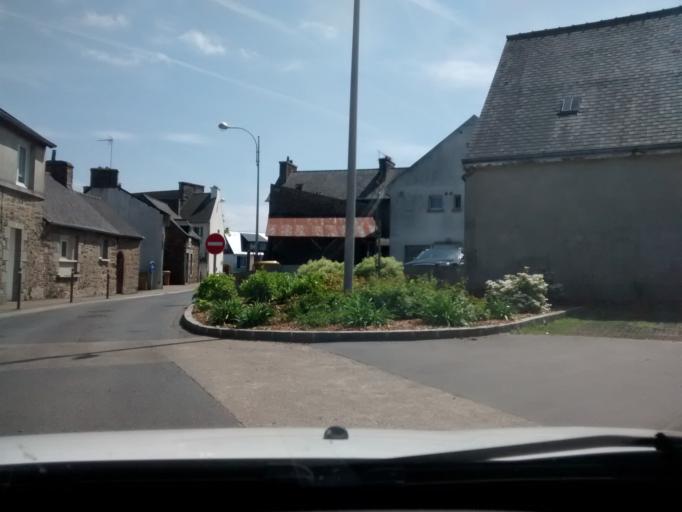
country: FR
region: Brittany
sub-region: Departement des Cotes-d'Armor
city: Langueux
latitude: 48.4952
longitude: -2.7146
